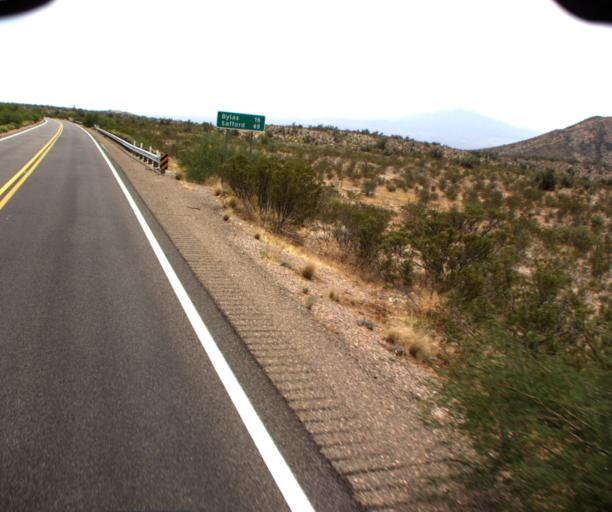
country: US
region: Arizona
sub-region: Gila County
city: Peridot
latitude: 33.2750
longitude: -110.3276
